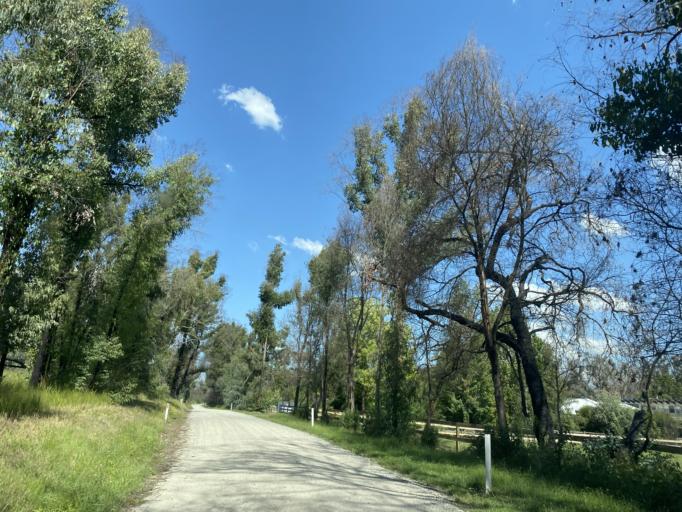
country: AU
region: Victoria
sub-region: Cardinia
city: Bunyip
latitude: -38.0041
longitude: 145.7381
